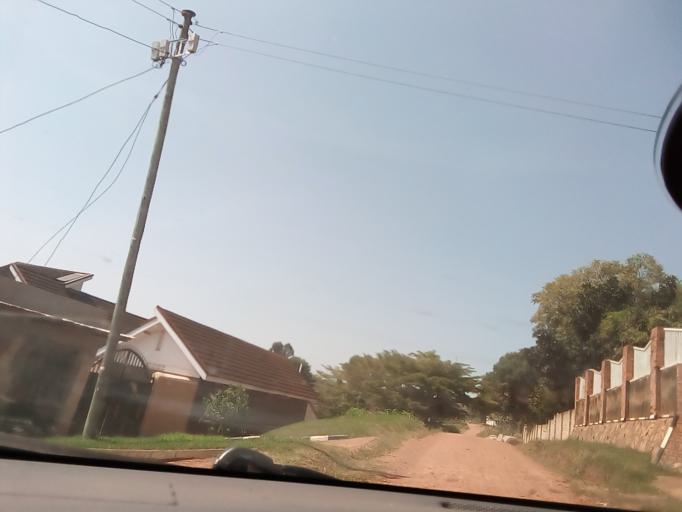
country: UG
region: Central Region
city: Masaka
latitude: -0.3485
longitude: 31.7429
